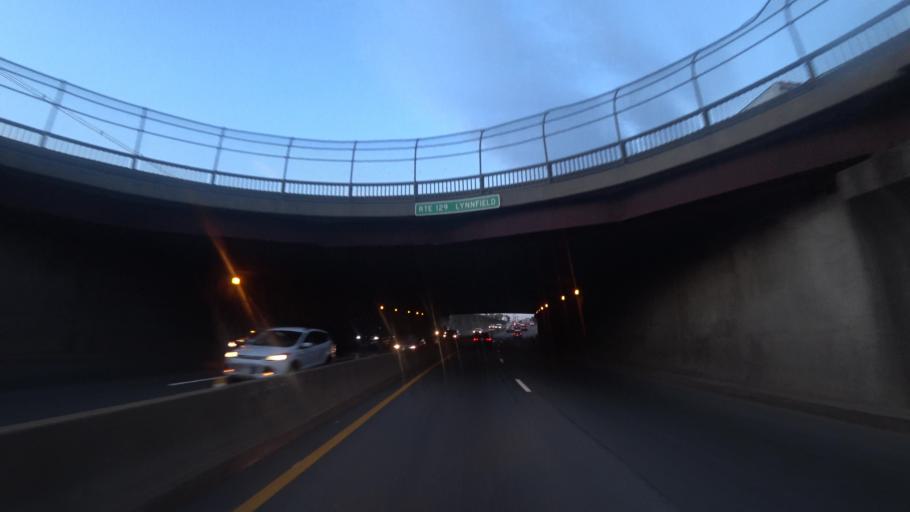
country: US
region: Massachusetts
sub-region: Essex County
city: Saugus
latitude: 42.5151
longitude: -71.0027
